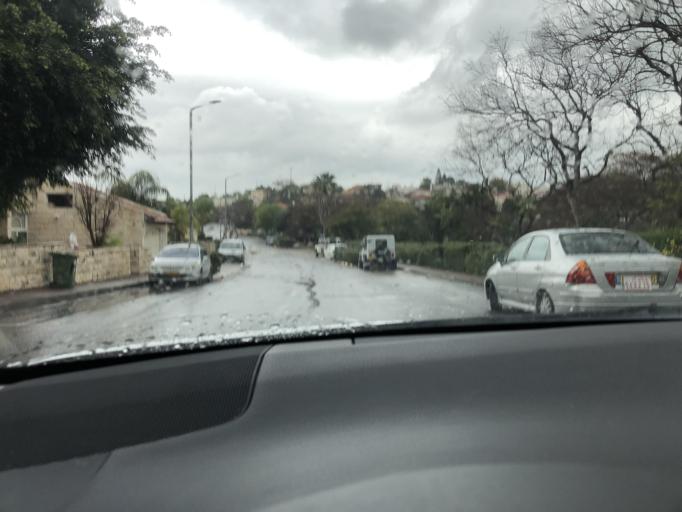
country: PS
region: West Bank
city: Azun Atme
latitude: 32.1119
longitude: 35.0293
